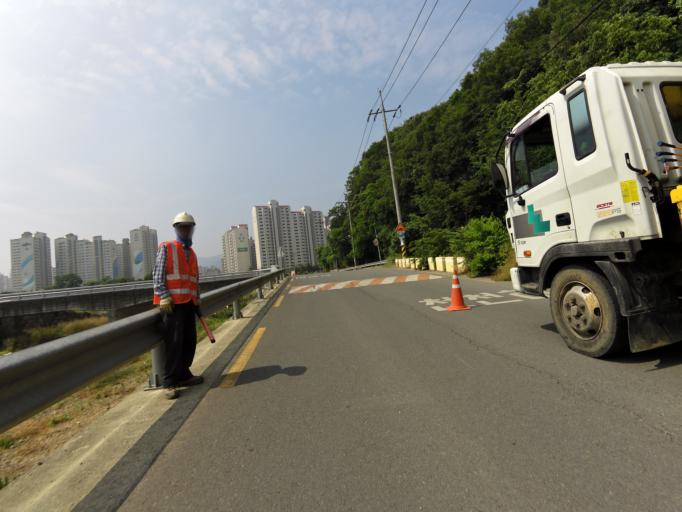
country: KR
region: Gyeongsangbuk-do
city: Gyeongsan-si
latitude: 35.8497
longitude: 128.7071
